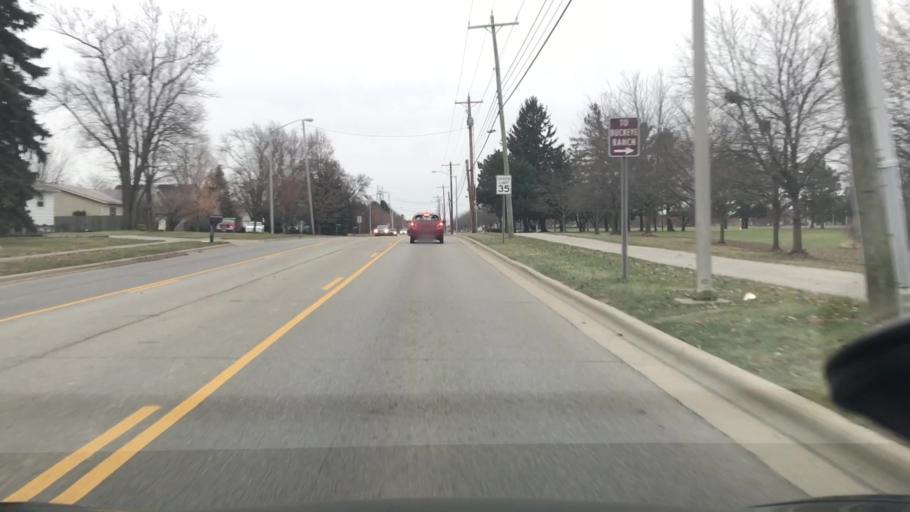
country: US
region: Ohio
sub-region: Franklin County
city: Grove City
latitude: 39.8484
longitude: -83.0719
